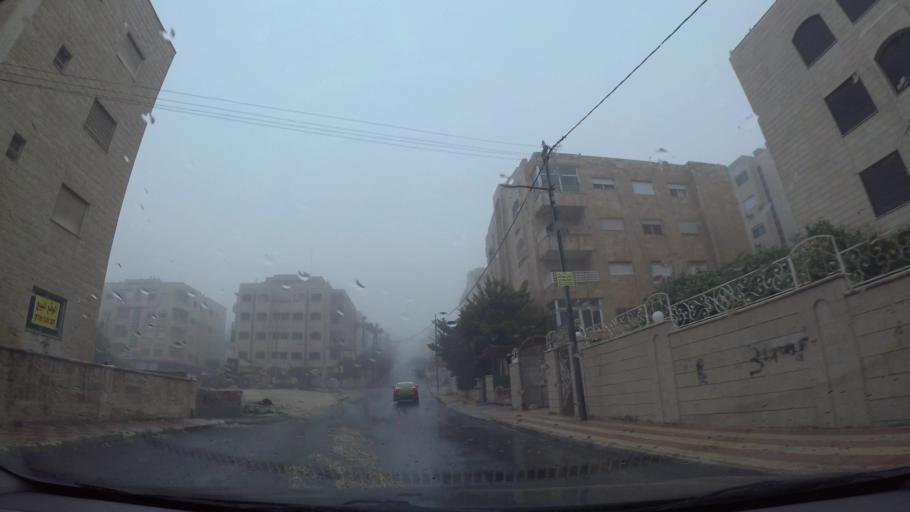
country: JO
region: Amman
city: Al Jubayhah
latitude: 32.0172
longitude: 35.8787
